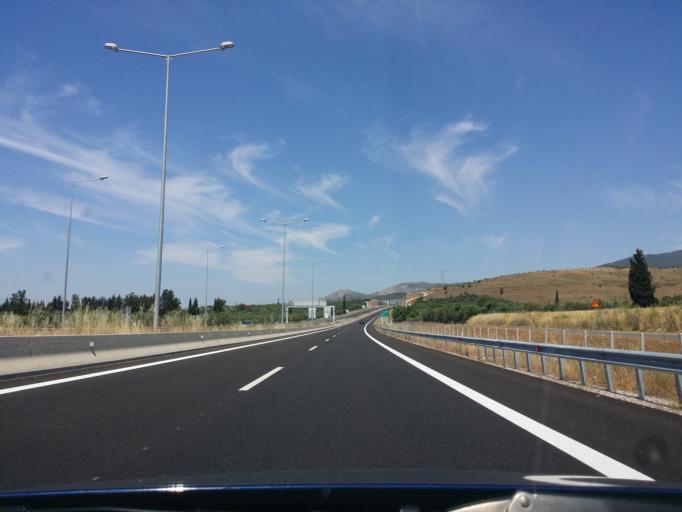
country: GR
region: West Greece
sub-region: Nomos Aitolias kai Akarnanias
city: Mesolongi
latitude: 38.3821
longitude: 21.4929
